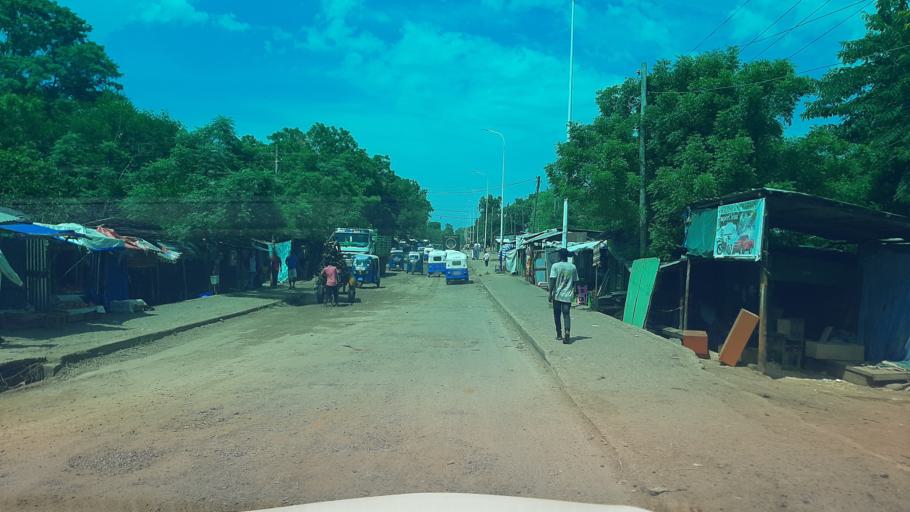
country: ET
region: Gambela
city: Gambela
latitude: 8.2368
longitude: 34.5835
